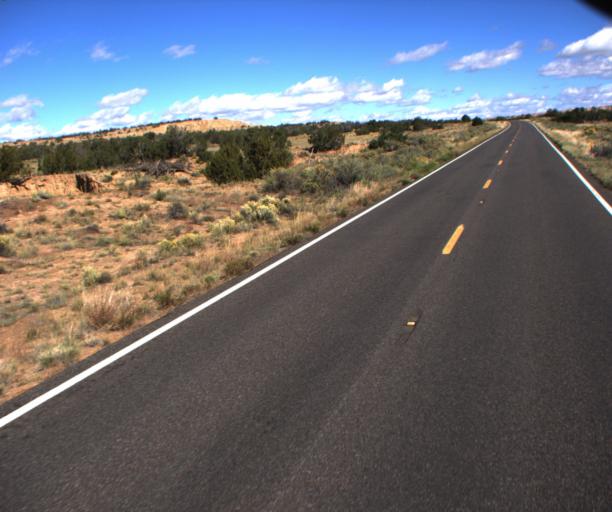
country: US
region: Arizona
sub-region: Apache County
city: Saint Johns
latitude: 34.7778
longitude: -109.2391
